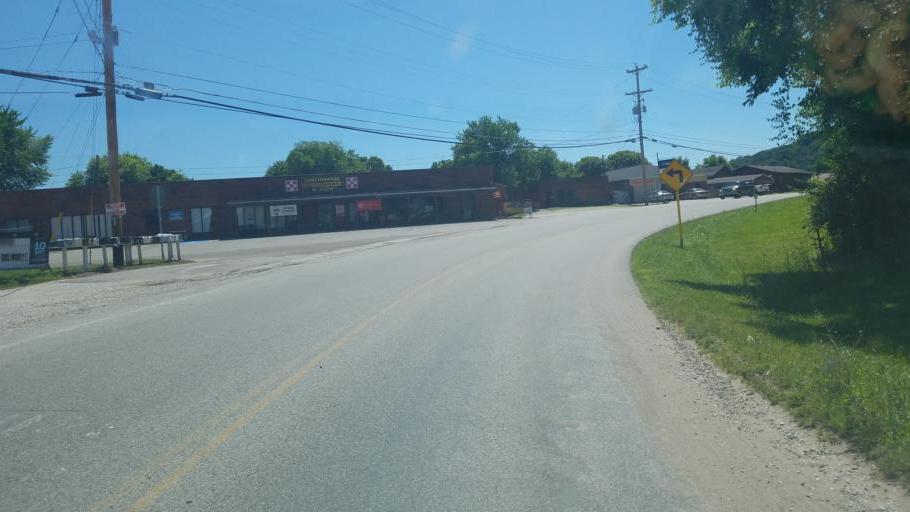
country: US
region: West Virginia
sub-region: Cabell County
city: Pea Ridge
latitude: 38.4428
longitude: -82.3555
